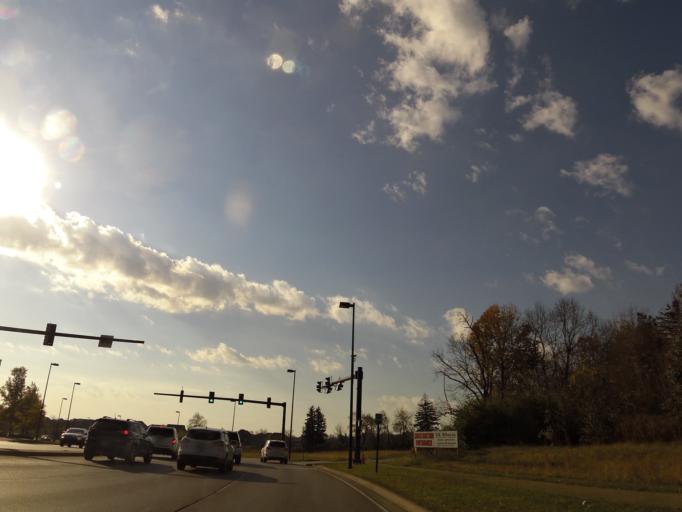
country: US
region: Kentucky
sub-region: Fayette County
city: Lexington-Fayette
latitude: 38.0399
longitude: -84.4290
